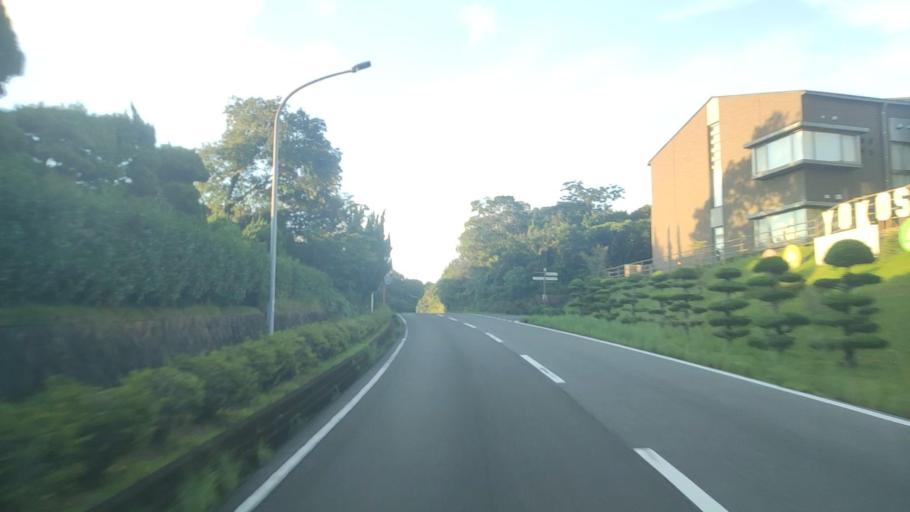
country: JP
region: Mie
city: Toba
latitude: 34.3189
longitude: 136.8167
